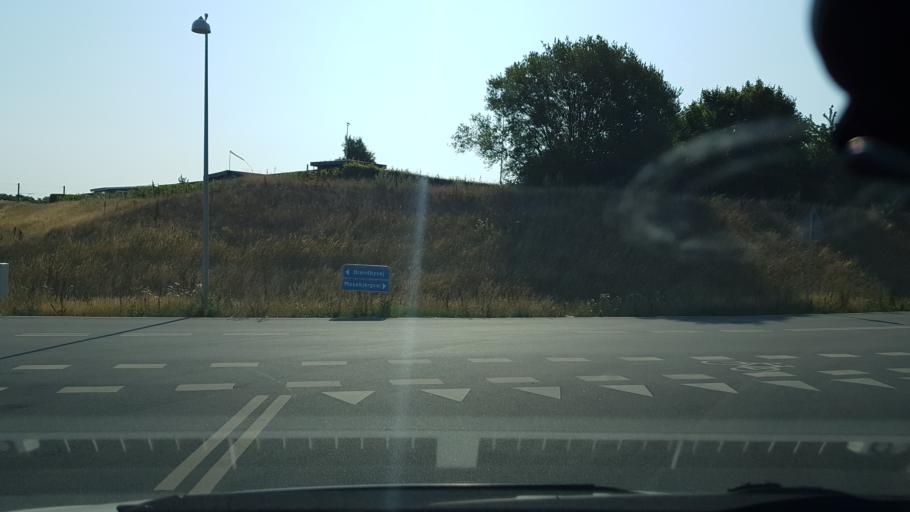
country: DK
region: Capital Region
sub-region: Brondby Kommune
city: Brondbyvester
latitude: 55.6407
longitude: 12.3899
